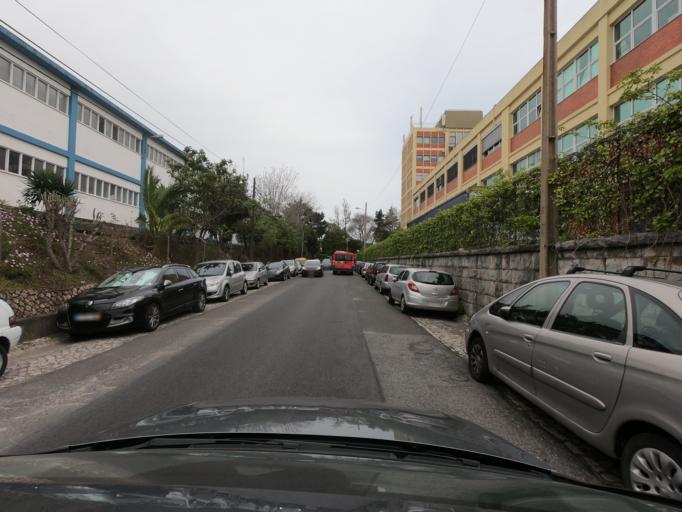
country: PT
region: Lisbon
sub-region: Oeiras
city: Barcarena
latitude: 38.7411
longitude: -9.2689
